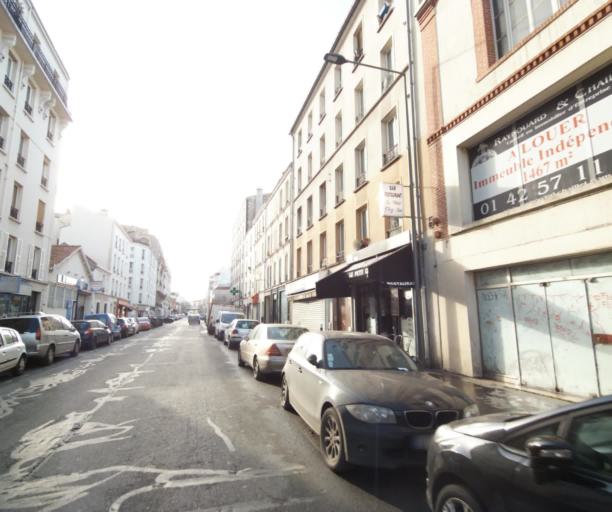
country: FR
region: Ile-de-France
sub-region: Paris
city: Saint-Ouen
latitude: 48.9052
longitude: 2.3327
